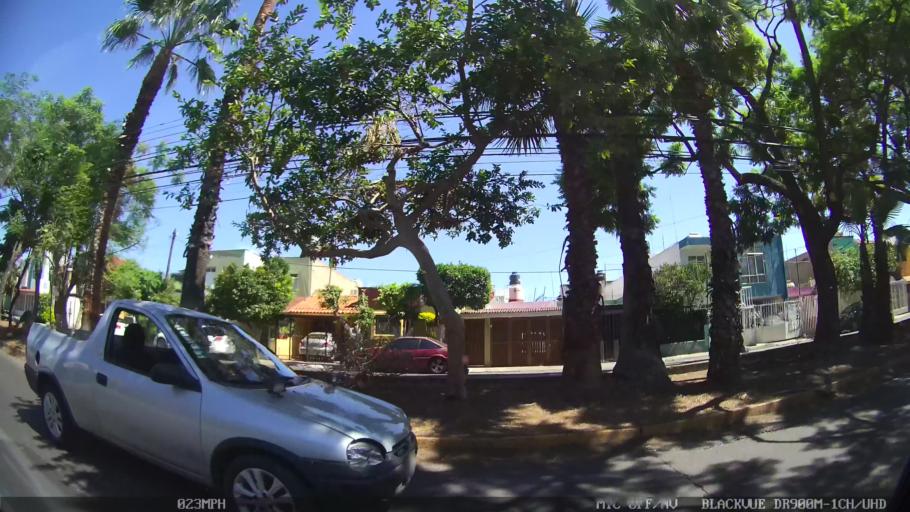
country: MX
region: Jalisco
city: Tlaquepaque
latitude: 20.6448
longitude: -103.2945
